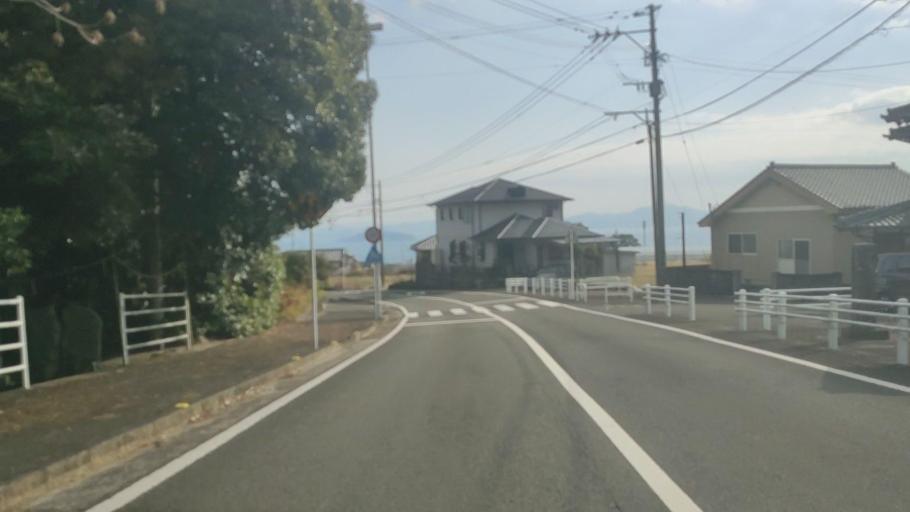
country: JP
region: Nagasaki
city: Shimabara
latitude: 32.6784
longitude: 130.2790
